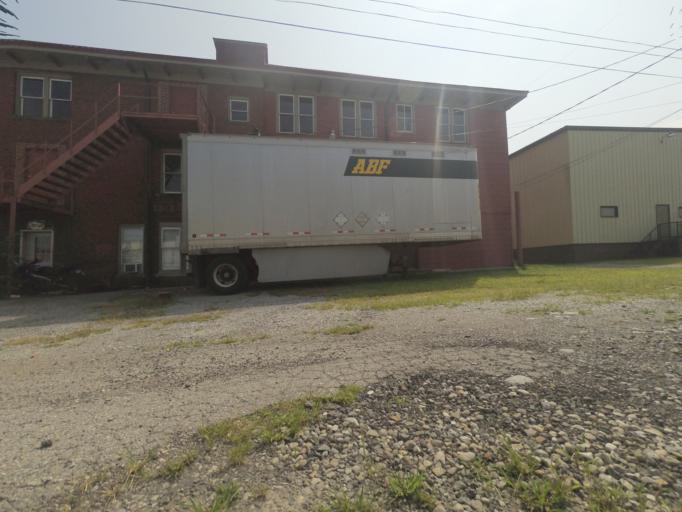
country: US
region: West Virginia
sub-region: Cabell County
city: Huntington
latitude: 38.4173
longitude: -82.4375
